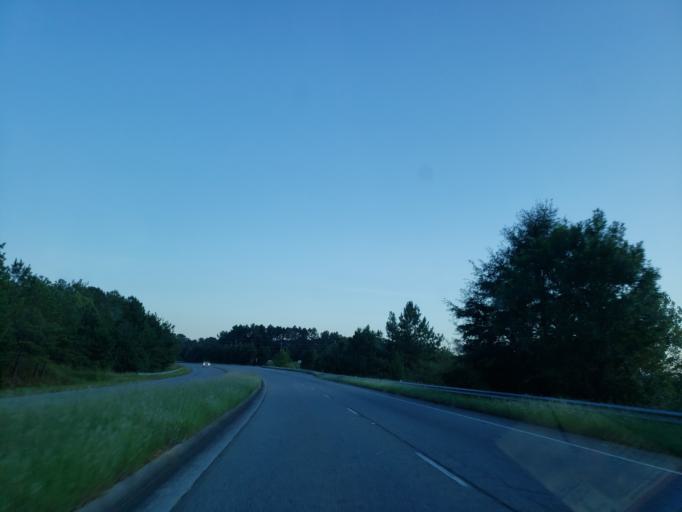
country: US
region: Georgia
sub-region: Polk County
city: Cedartown
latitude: 34.0917
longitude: -85.2372
